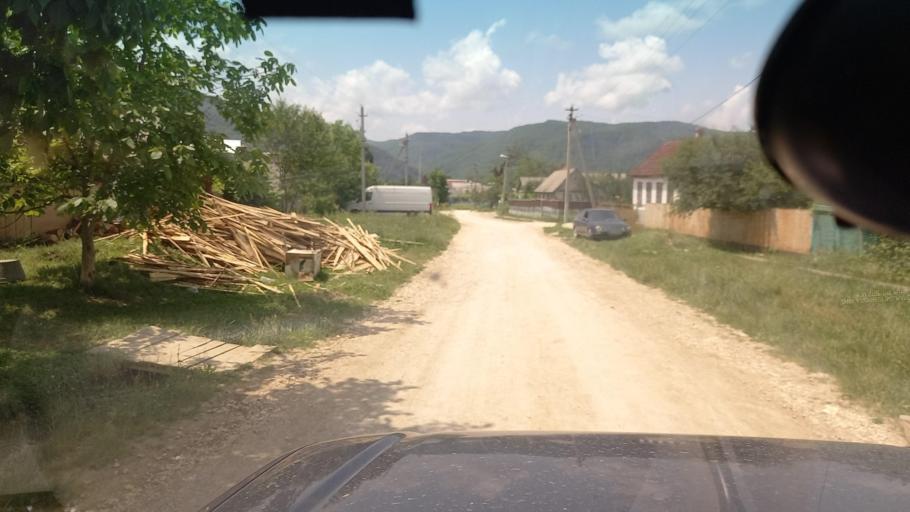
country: RU
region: Adygeya
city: Kamennomostskiy
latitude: 44.2897
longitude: 40.1899
